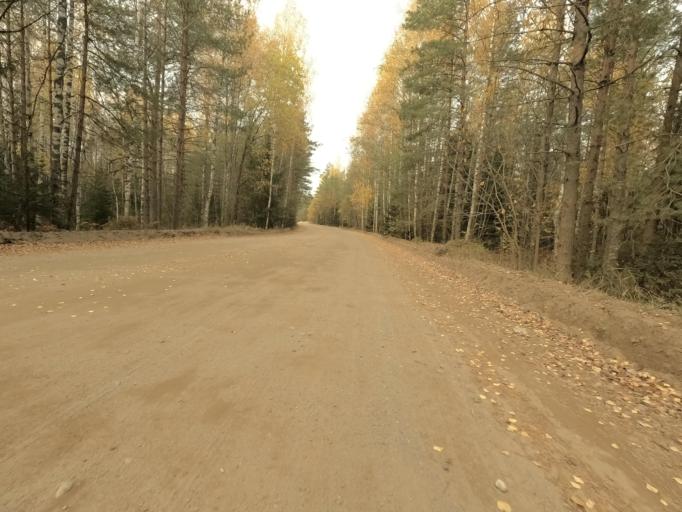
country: RU
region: Leningrad
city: Priladozhskiy
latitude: 59.6866
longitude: 31.3620
